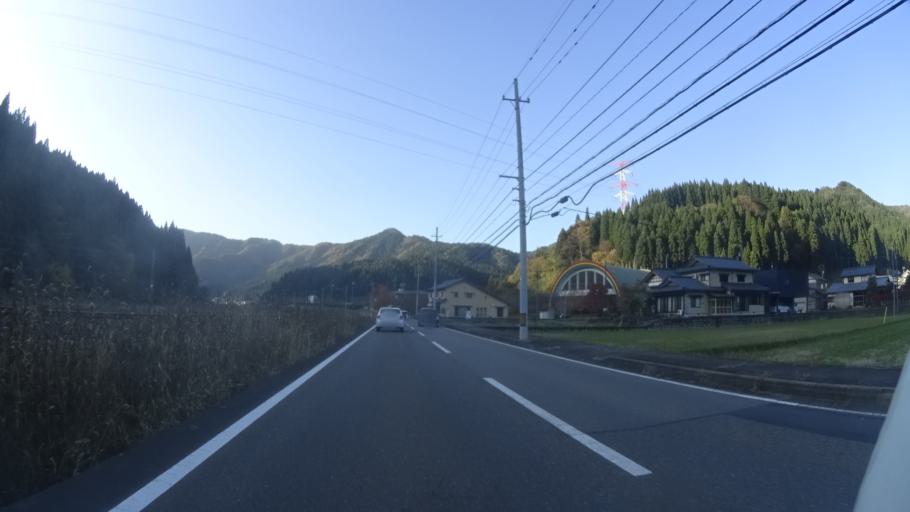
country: JP
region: Fukui
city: Ono
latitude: 36.0034
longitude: 136.4037
